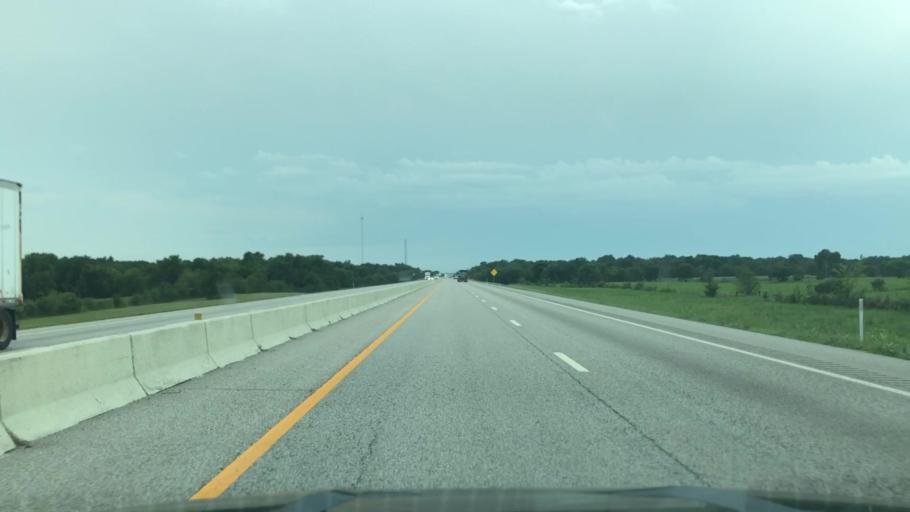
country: US
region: Oklahoma
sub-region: Craig County
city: Vinita
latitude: 36.5903
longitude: -95.1978
